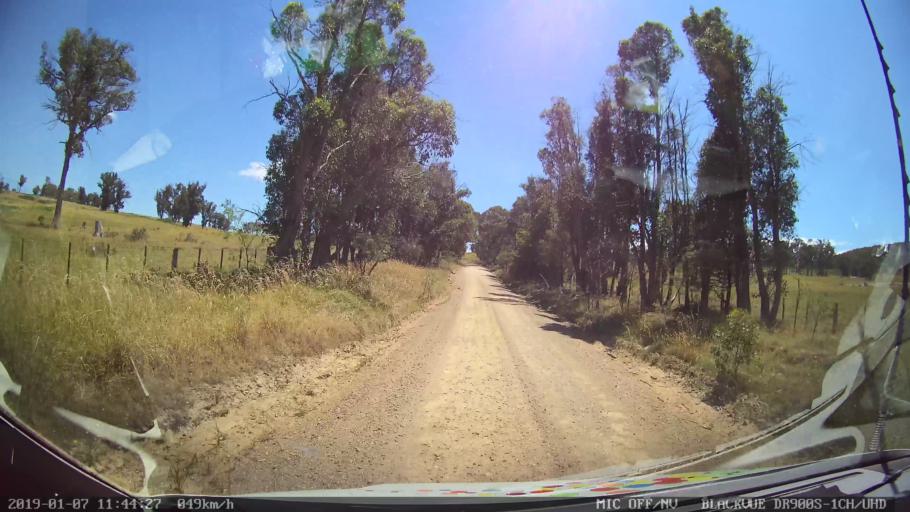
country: AU
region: New South Wales
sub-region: Guyra
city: Guyra
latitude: -30.3526
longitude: 151.6063
